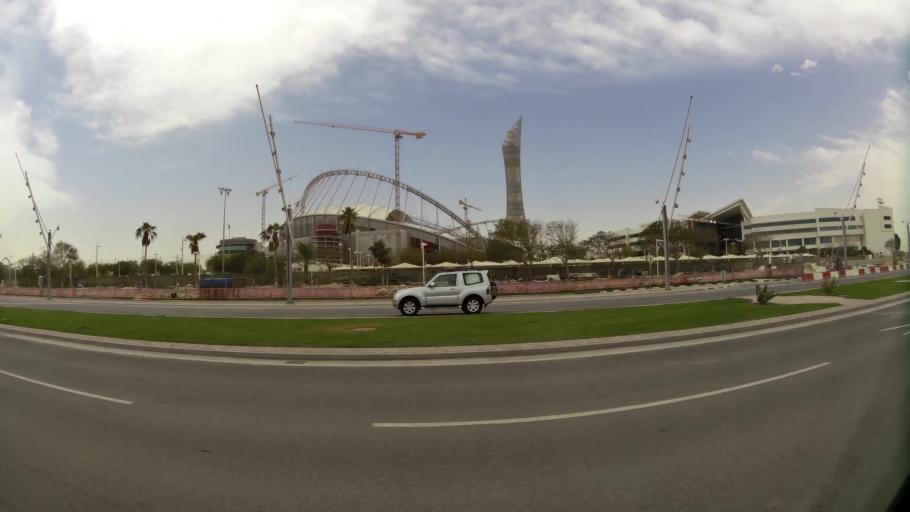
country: QA
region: Baladiyat ar Rayyan
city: Ar Rayyan
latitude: 25.2668
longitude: 51.4510
